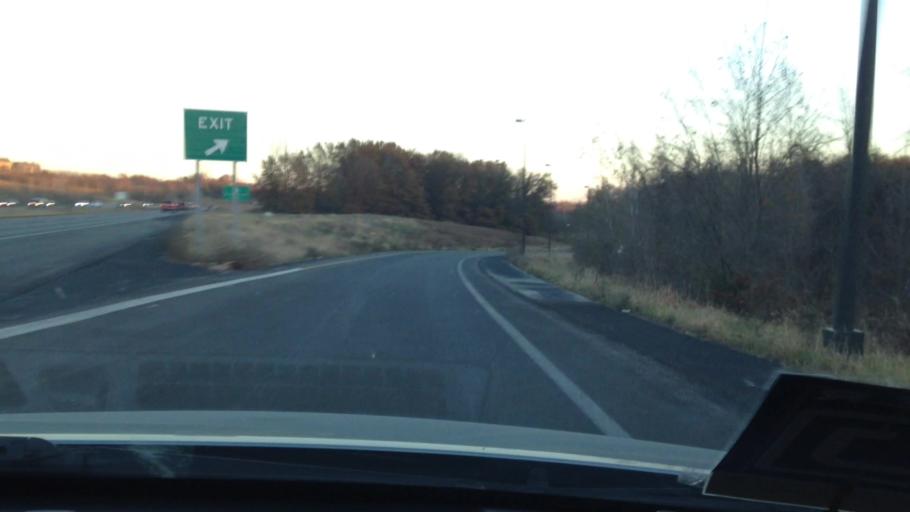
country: US
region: Missouri
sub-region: Clay County
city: Gladstone
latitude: 39.2591
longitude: -94.5620
